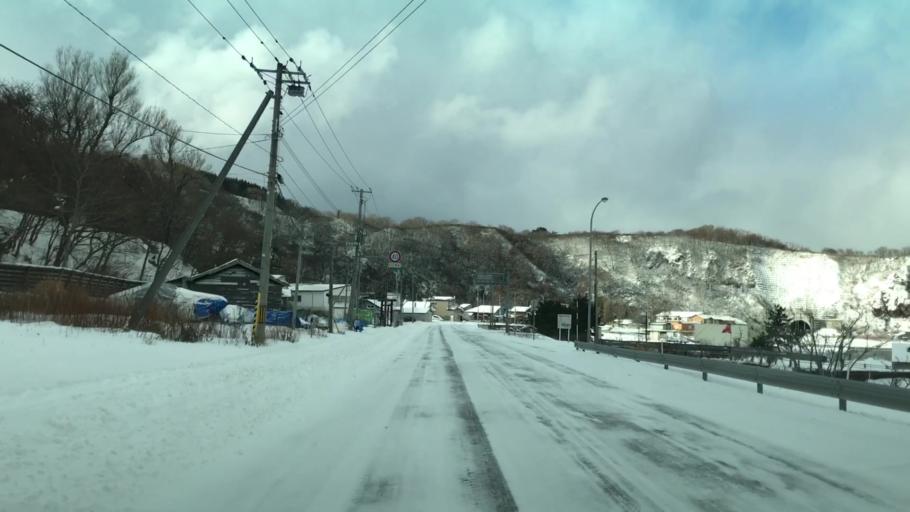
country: JP
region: Hokkaido
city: Iwanai
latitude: 43.3300
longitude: 140.3999
